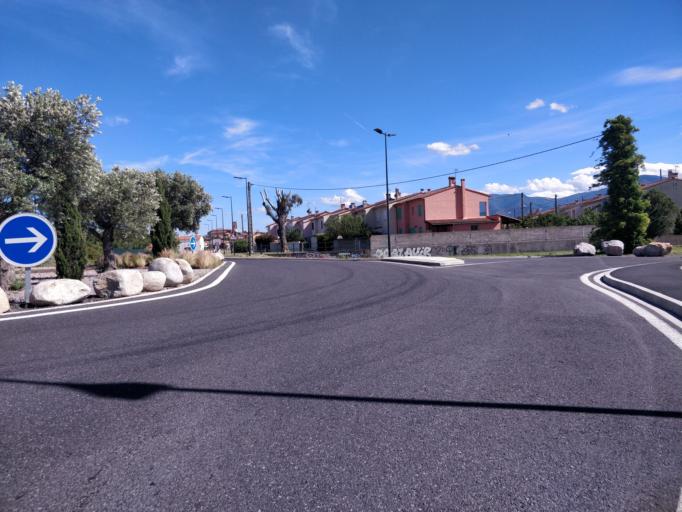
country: FR
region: Languedoc-Roussillon
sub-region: Departement des Pyrenees-Orientales
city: Elne
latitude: 42.6068
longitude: 2.9648
